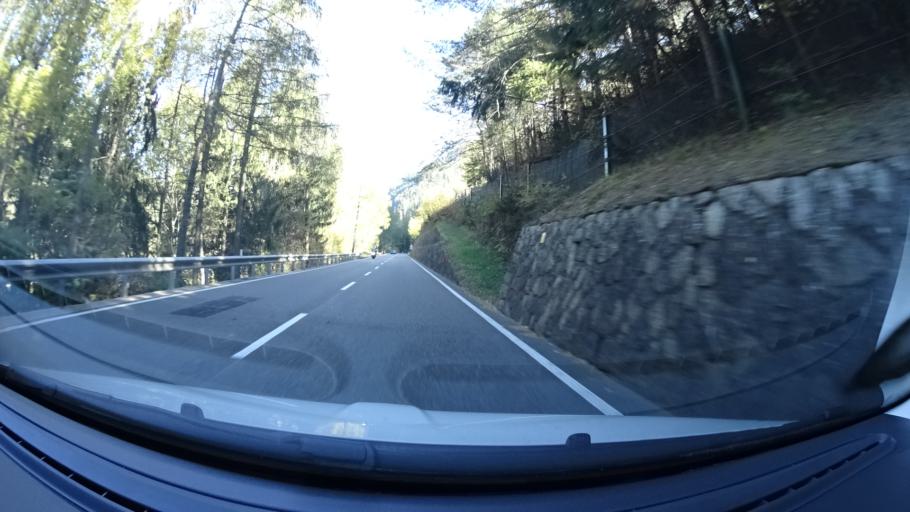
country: IT
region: Trentino-Alto Adige
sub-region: Bolzano
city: Anterivo
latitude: 46.2608
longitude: 11.3749
